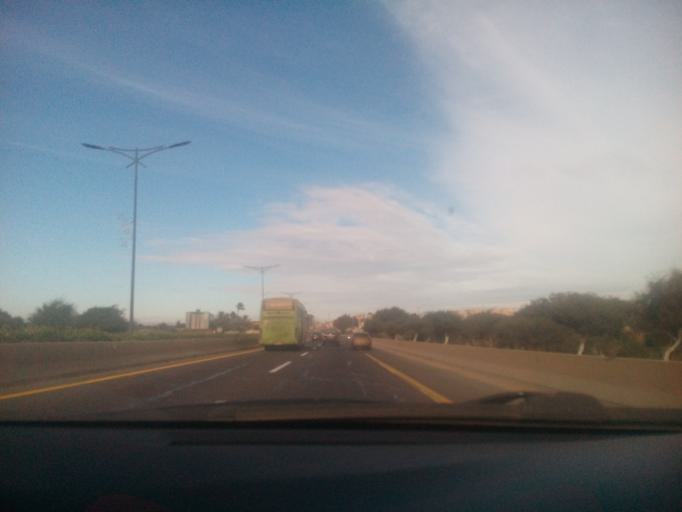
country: DZ
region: Oran
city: Es Senia
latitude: 35.6025
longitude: -0.5748
